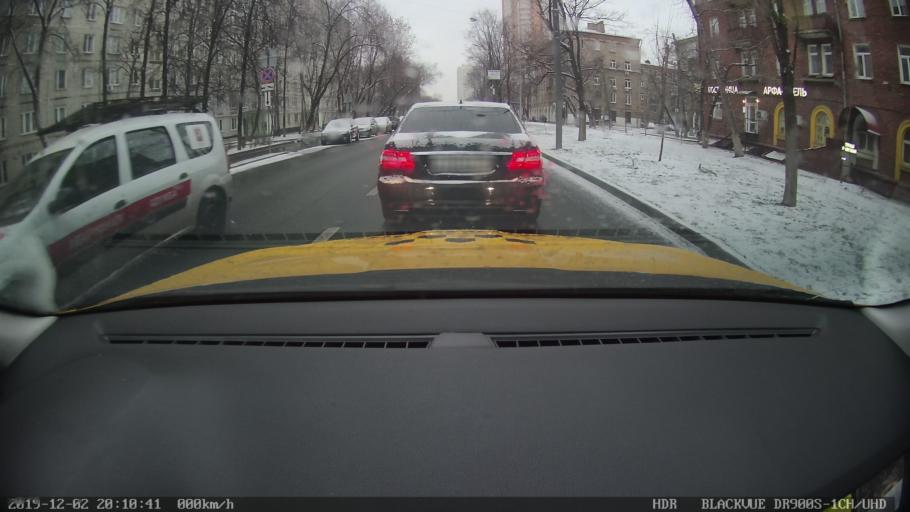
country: RU
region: Moscow
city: Novokuz'minki
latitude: 55.7144
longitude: 37.7906
